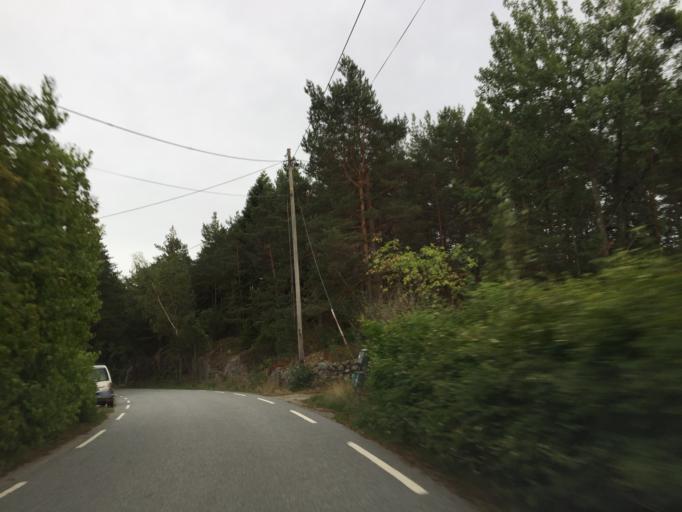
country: NO
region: Ostfold
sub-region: Hvaler
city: Skjaerhalden
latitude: 59.0637
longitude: 11.0062
